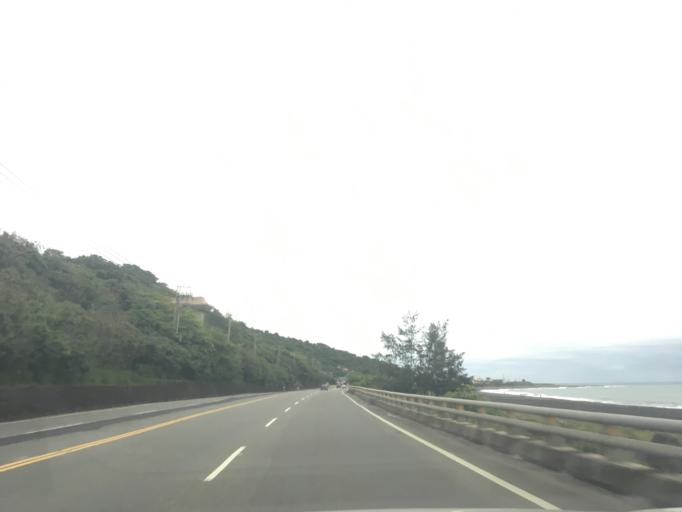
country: TW
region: Taiwan
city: Hengchun
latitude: 22.3491
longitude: 120.9004
